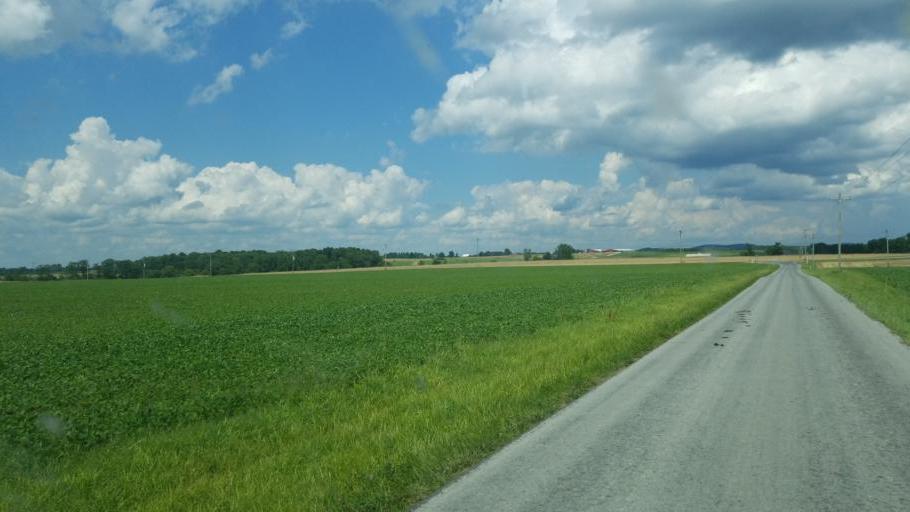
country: US
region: Ohio
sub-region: Highland County
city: Greenfield
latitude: 39.2441
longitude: -83.4417
